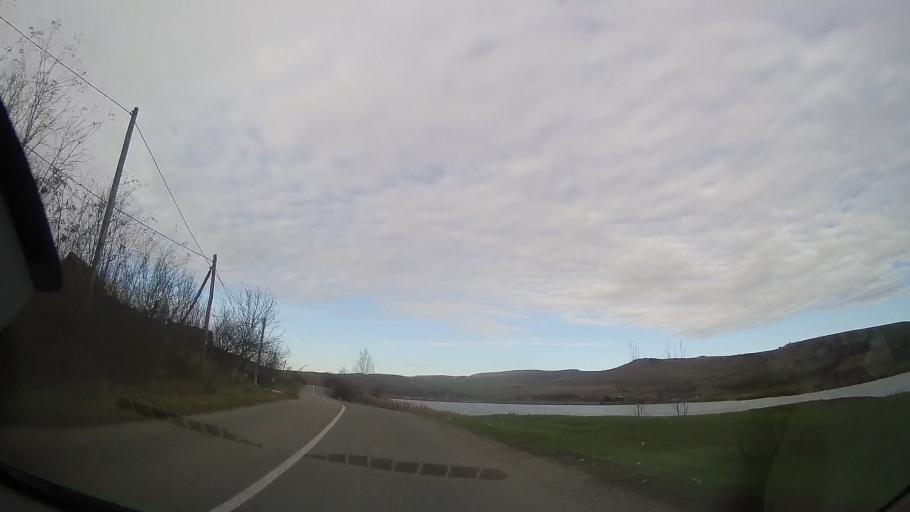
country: RO
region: Cluj
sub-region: Comuna Geaca
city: Geaca
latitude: 46.8415
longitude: 24.1252
